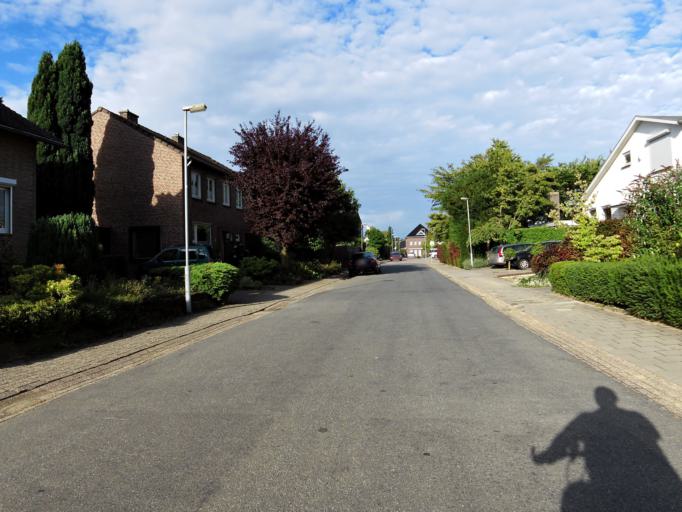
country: NL
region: Limburg
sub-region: Gemeente Voerendaal
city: Kunrade
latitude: 50.8775
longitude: 5.9314
